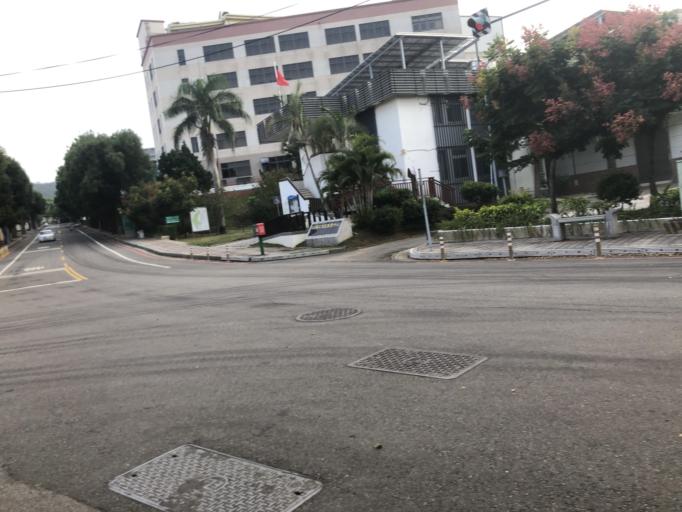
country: TW
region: Taiwan
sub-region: Miaoli
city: Miaoli
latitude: 24.4815
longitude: 120.7922
